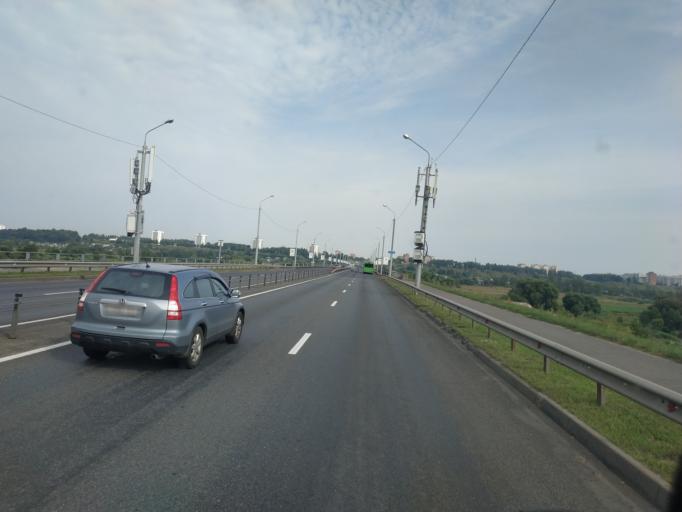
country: BY
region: Mogilev
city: Mahilyow
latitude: 53.8890
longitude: 30.3768
